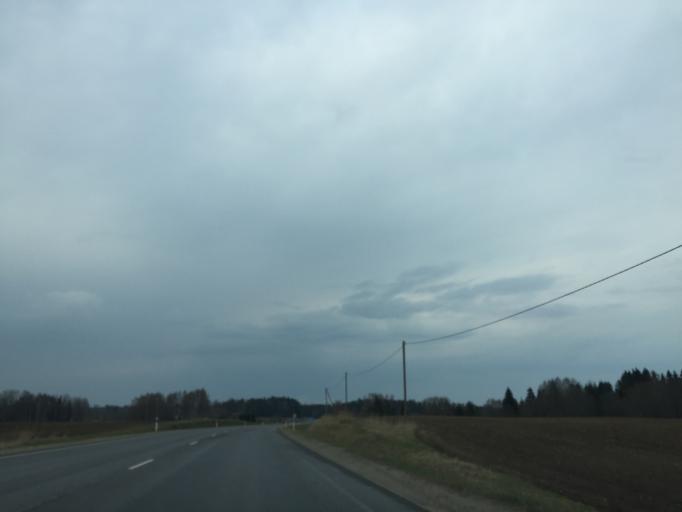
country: EE
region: Tartu
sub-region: UElenurme vald
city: Ulenurme
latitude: 58.0888
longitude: 26.7343
